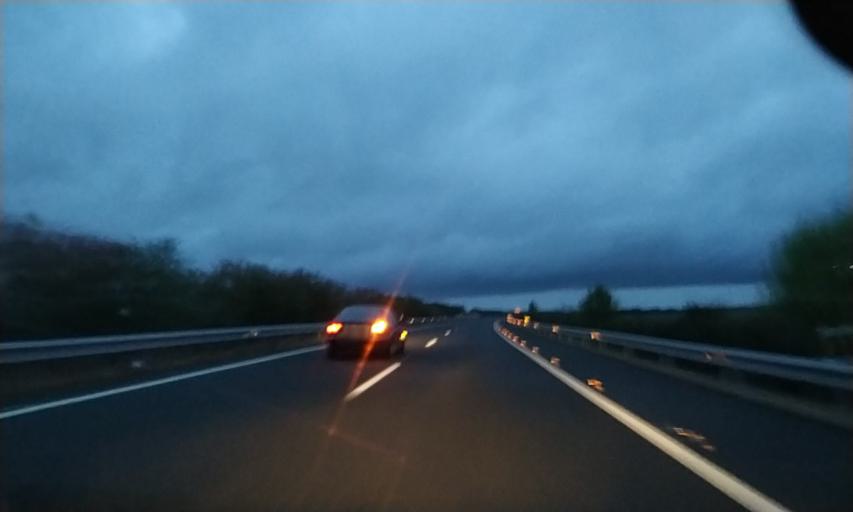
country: ES
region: Extremadura
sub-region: Provincia de Caceres
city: Aldea del Cano
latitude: 39.2877
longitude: -6.3301
